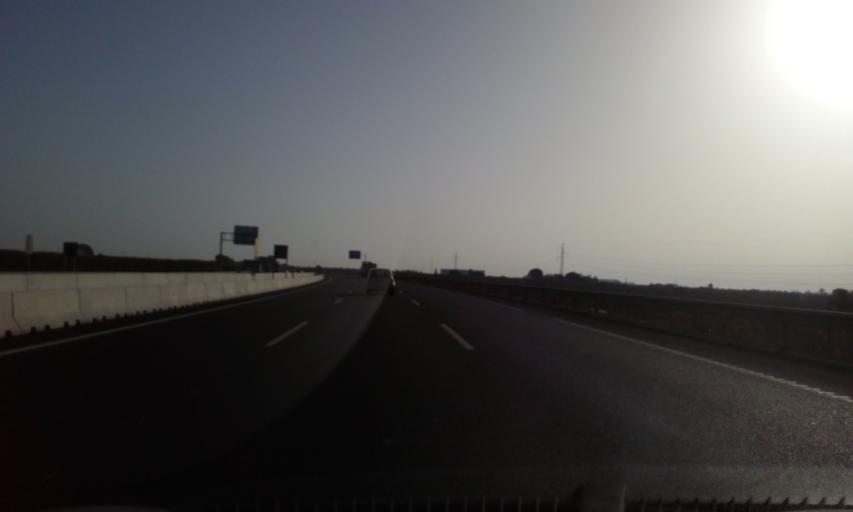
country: ES
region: Andalusia
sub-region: Provincia de Sevilla
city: Benacazon
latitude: 37.3583
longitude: -6.1916
